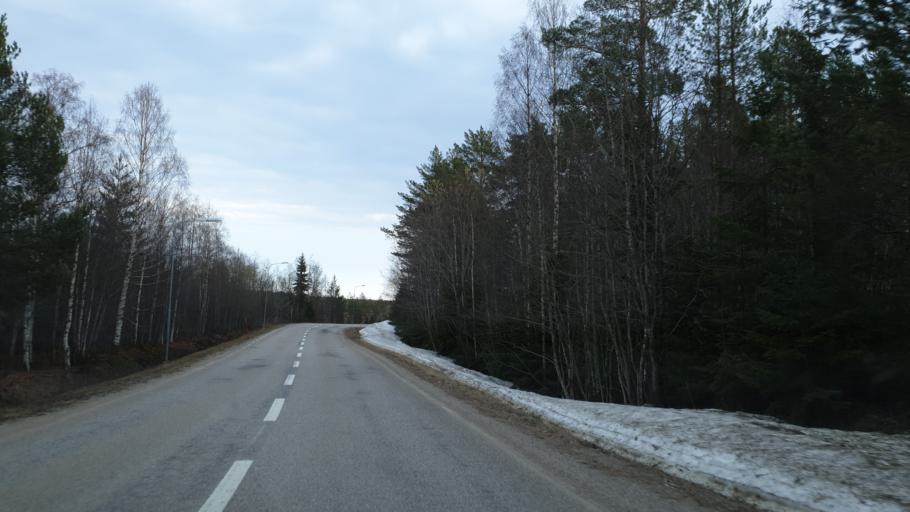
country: SE
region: Gaevleborg
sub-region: Nordanstigs Kommun
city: Bergsjoe
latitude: 61.9620
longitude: 17.3180
